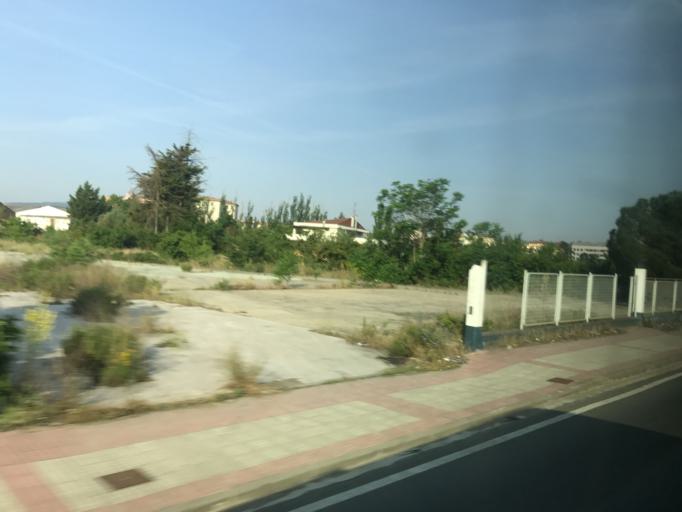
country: ES
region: Castille and Leon
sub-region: Provincia de Burgos
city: Miranda de Ebro
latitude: 42.6913
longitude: -2.9471
